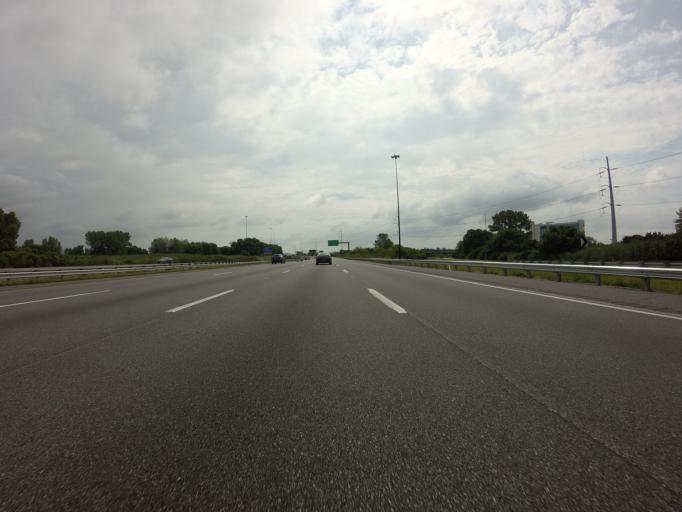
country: US
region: Pennsylvania
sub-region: Delaware County
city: Folcroft
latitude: 39.8758
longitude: -75.2767
